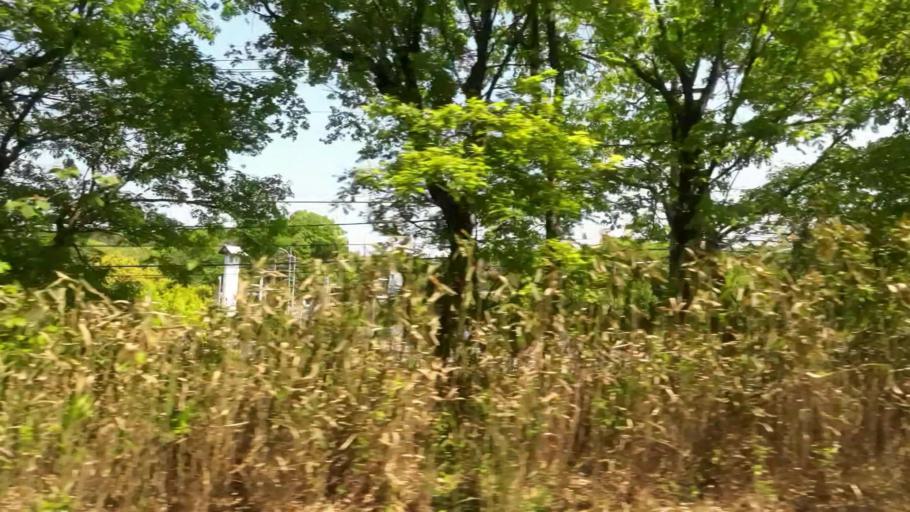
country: JP
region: Ehime
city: Saijo
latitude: 33.9922
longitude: 133.0494
